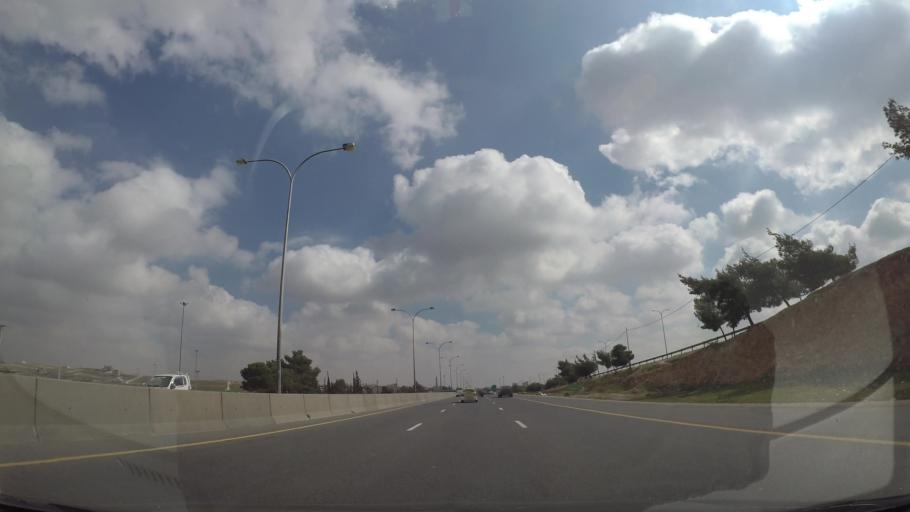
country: JO
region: Amman
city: Jawa
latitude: 31.7974
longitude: 35.9186
